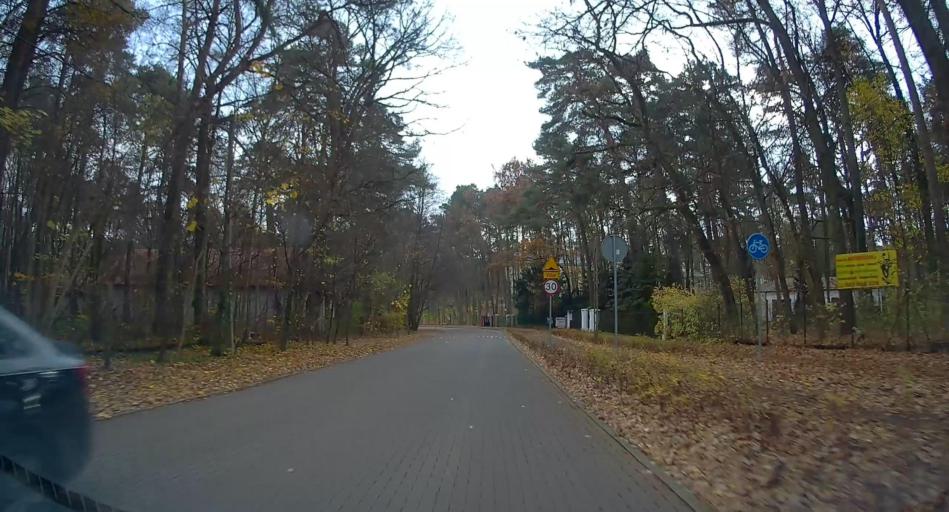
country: PL
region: Masovian Voivodeship
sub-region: Powiat piaseczynski
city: Piaseczno
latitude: 52.0553
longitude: 21.0194
